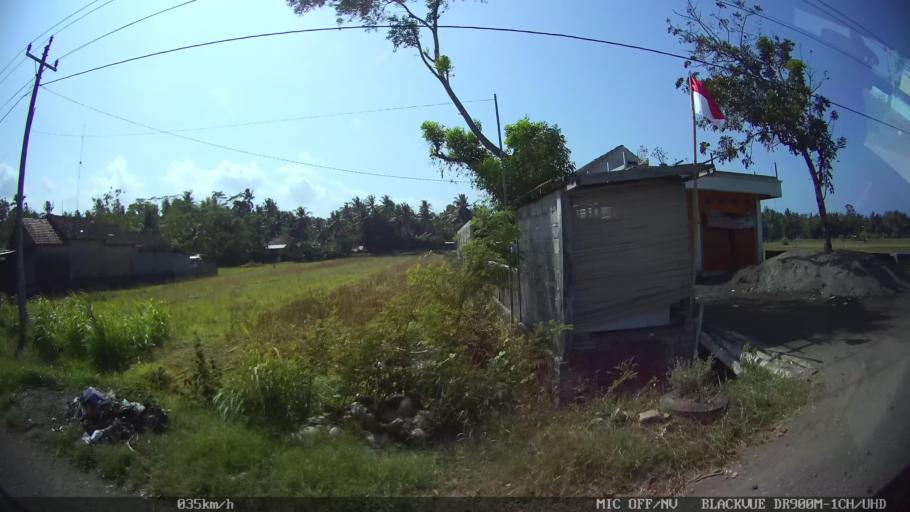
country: ID
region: Daerah Istimewa Yogyakarta
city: Srandakan
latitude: -7.9572
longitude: 110.2155
